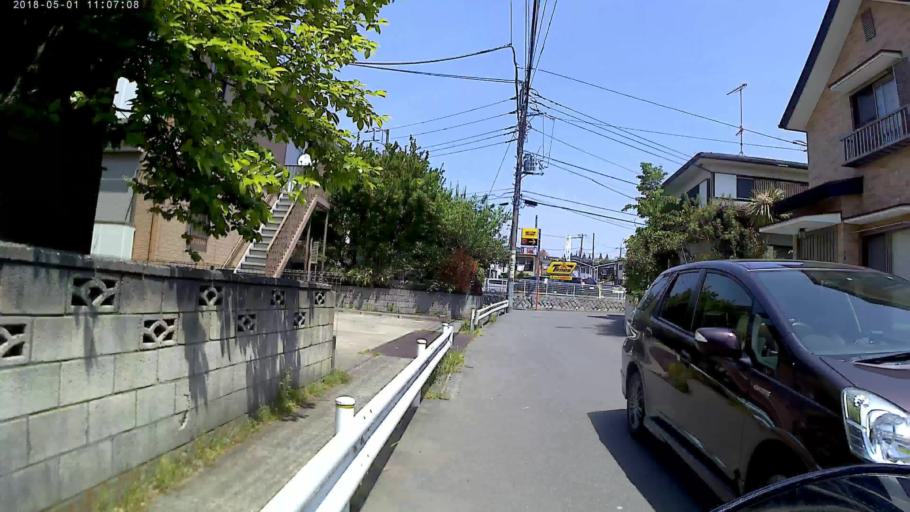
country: JP
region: Kanagawa
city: Minami-rinkan
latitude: 35.4834
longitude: 139.5330
